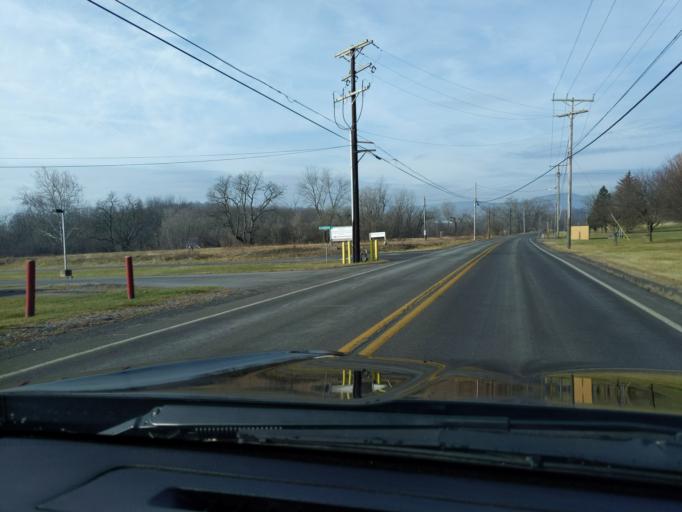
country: US
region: Pennsylvania
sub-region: Blair County
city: Duncansville
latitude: 40.4383
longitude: -78.4157
